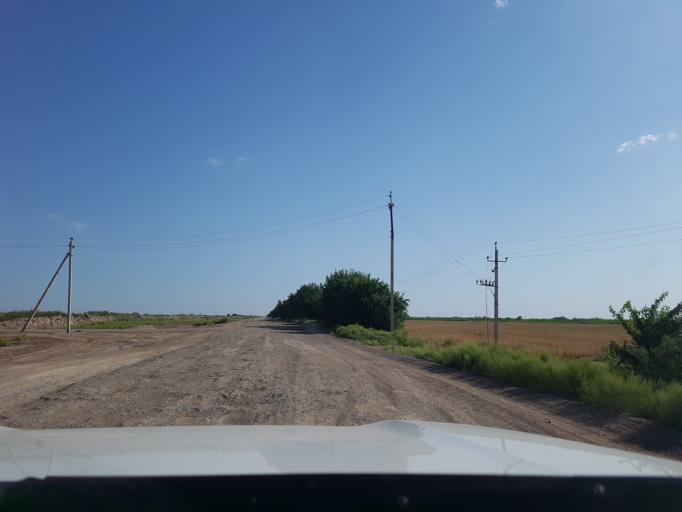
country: TM
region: Dasoguz
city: Koeneuergench
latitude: 41.9341
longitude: 58.7142
